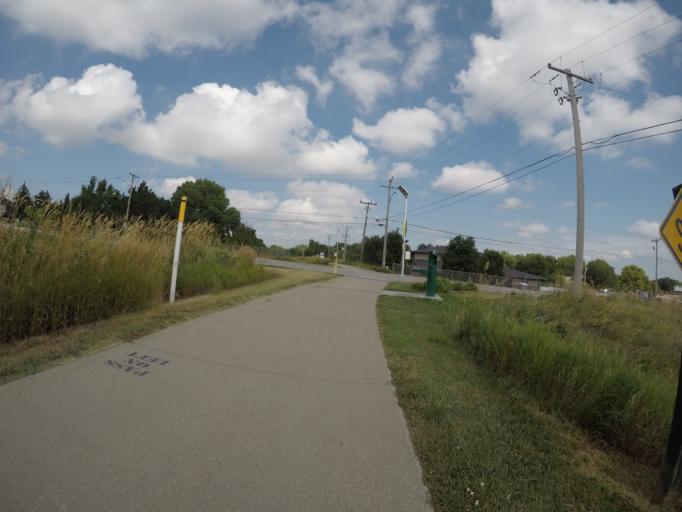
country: US
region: Nebraska
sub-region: Buffalo County
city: Kearney
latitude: 40.7009
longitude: -99.1225
